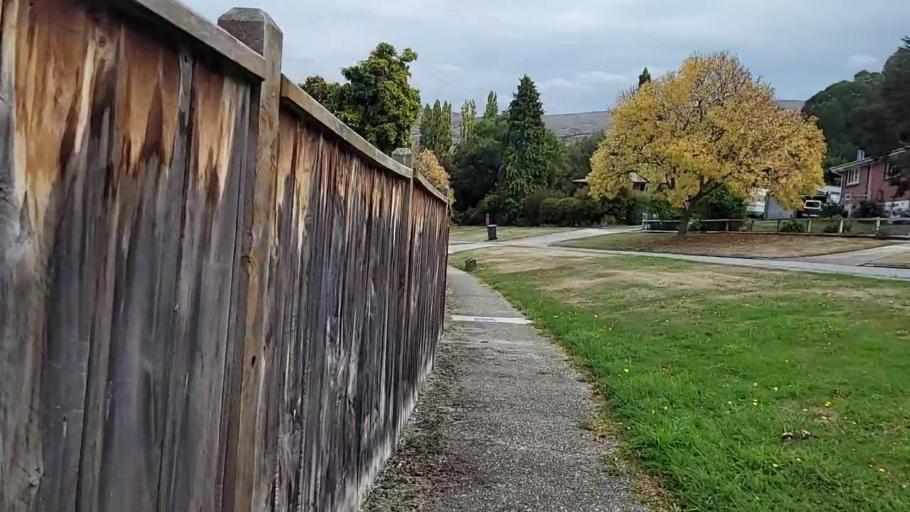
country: NZ
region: Otago
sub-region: Queenstown-Lakes District
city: Kingston
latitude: -45.4779
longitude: 169.3140
